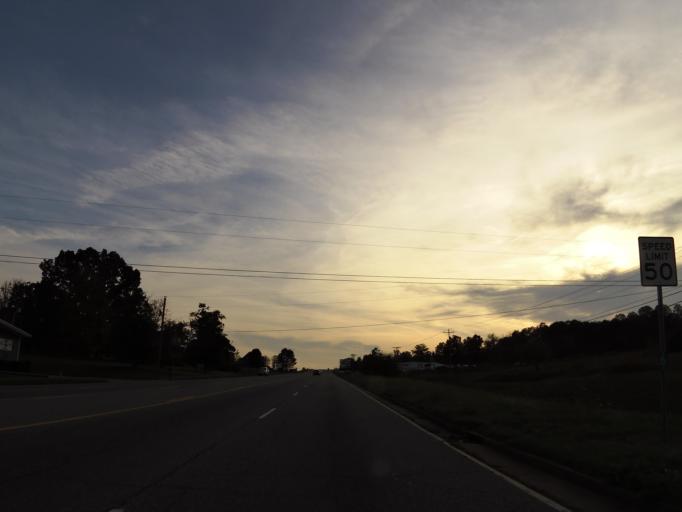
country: US
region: Tennessee
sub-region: Blount County
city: Maryville
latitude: 35.6967
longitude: -84.0458
